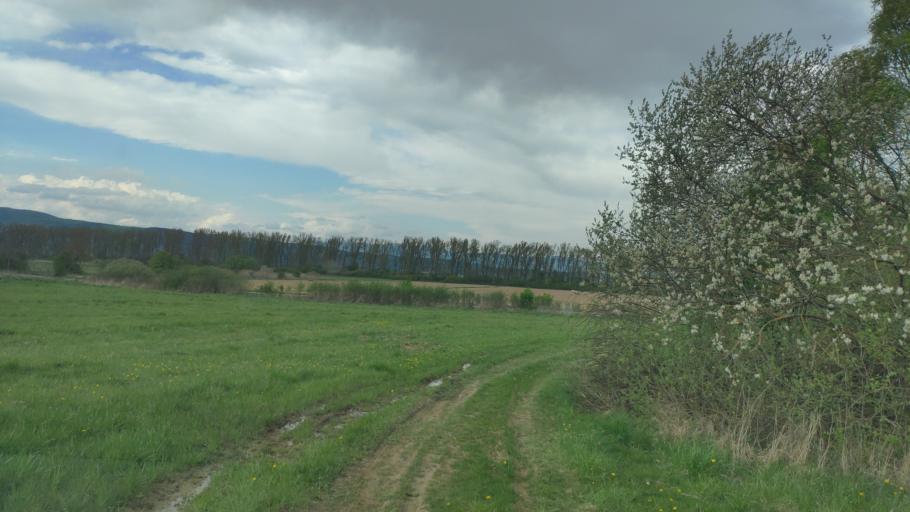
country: SK
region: Kosicky
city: Moldava nad Bodvou
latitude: 48.5592
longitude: 20.9556
